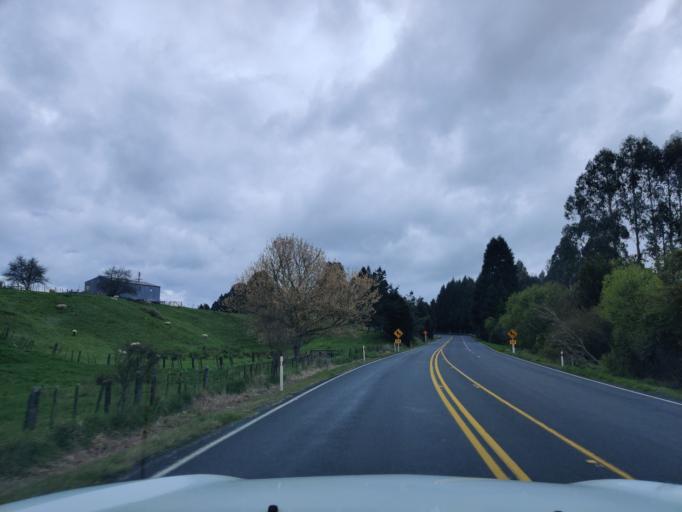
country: NZ
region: Waikato
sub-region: Otorohanga District
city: Otorohanga
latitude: -38.5013
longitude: 175.2023
